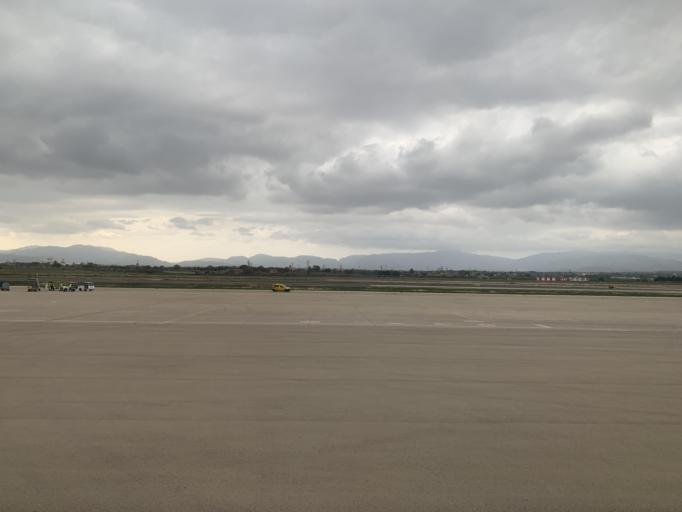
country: ES
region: Balearic Islands
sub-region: Illes Balears
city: s'Arenal
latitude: 39.5543
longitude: 2.7342
